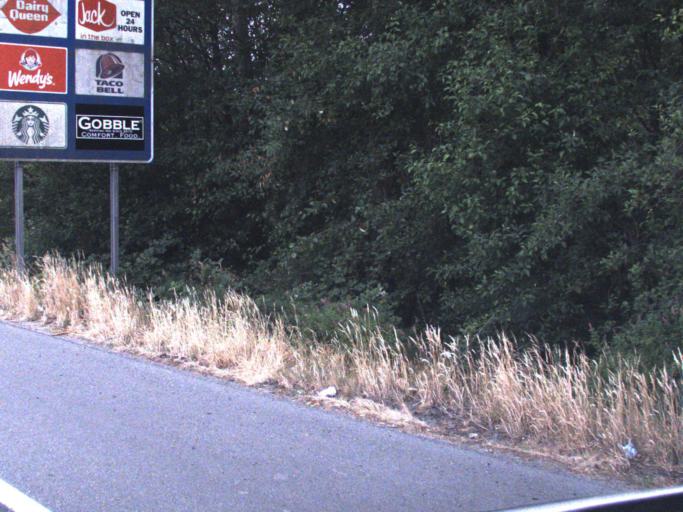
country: US
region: Washington
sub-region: King County
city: Woodinville
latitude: 47.7719
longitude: -122.1555
